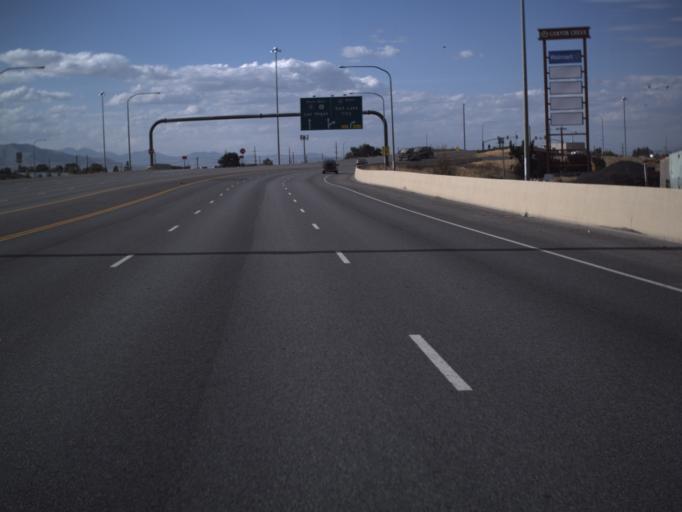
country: US
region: Utah
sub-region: Utah County
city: Spanish Fork
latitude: 40.1249
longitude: -111.6457
